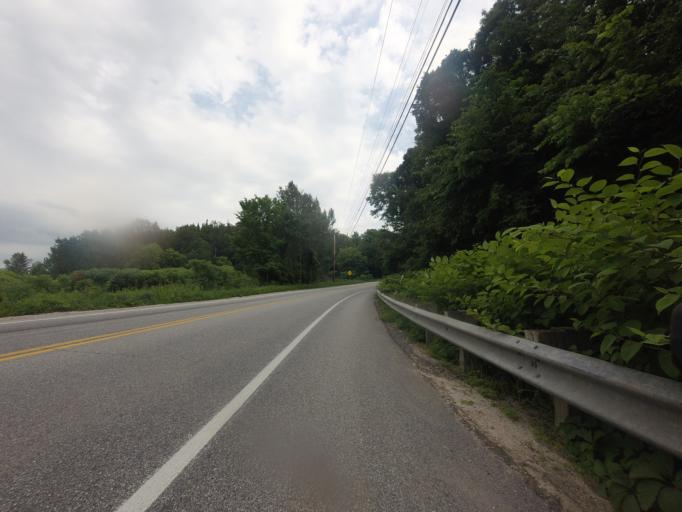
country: CA
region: Quebec
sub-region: Outaouais
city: Wakefield
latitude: 45.6867
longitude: -75.9303
